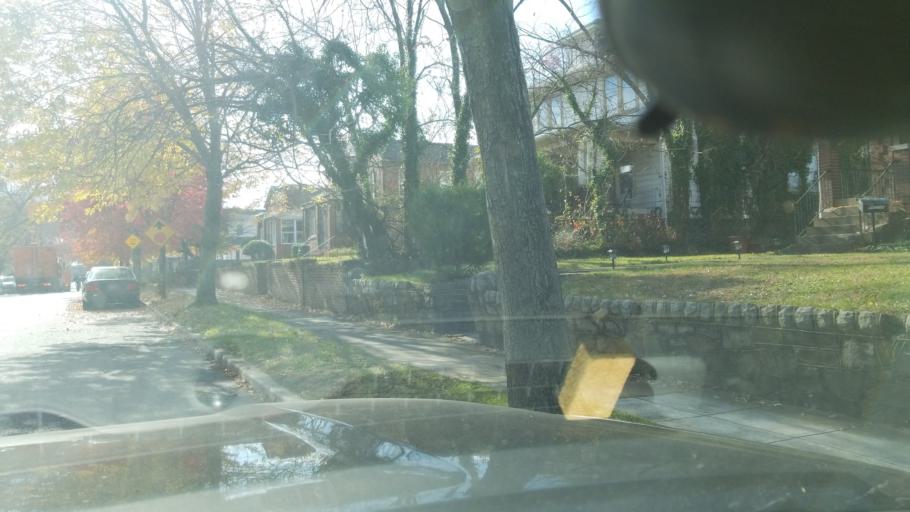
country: US
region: Maryland
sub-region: Prince George's County
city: Chillum
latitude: 38.9586
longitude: -77.0063
